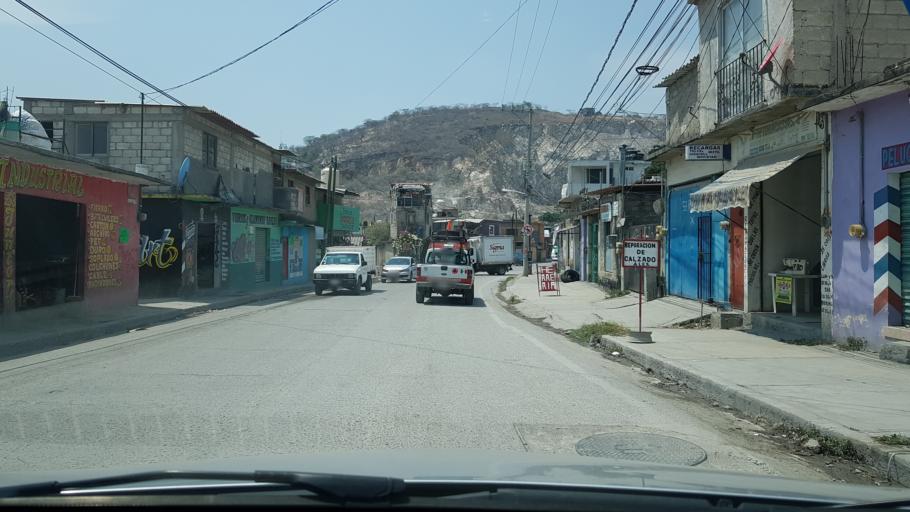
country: MX
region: Morelos
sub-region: Jiutepec
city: Calera Chica
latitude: 18.8592
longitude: -99.1786
